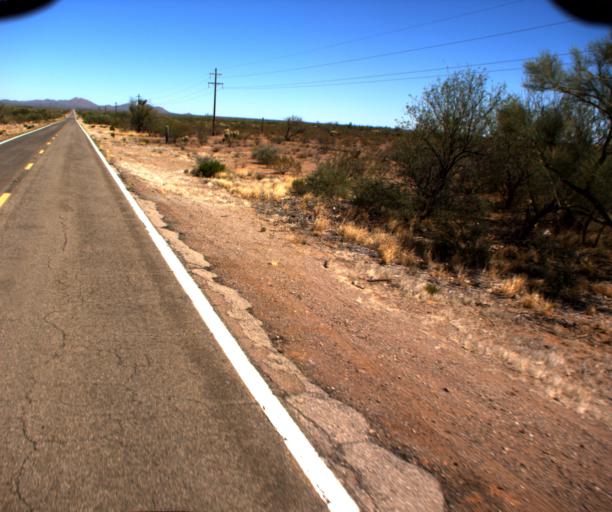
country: US
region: Arizona
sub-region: Pima County
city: Sells
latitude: 32.0841
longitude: -112.0527
